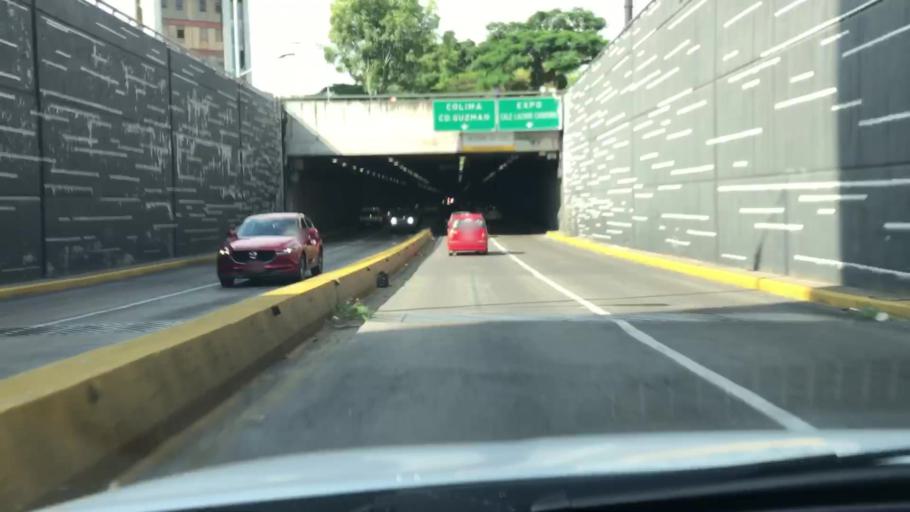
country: MX
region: Jalisco
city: Guadalajara
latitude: 20.6808
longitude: -103.3832
